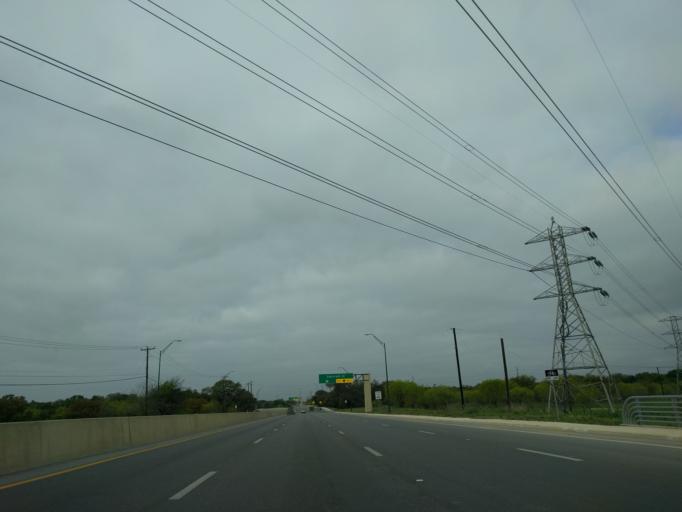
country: US
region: Texas
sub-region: Bexar County
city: Alamo Heights
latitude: 29.5472
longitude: -98.4462
